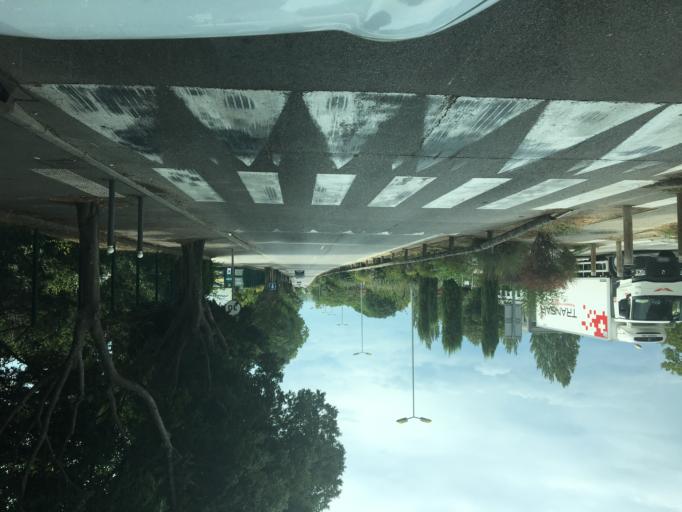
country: FR
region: Provence-Alpes-Cote d'Azur
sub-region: Departement des Bouches-du-Rhone
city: Cabries
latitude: 43.4871
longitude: 5.3786
